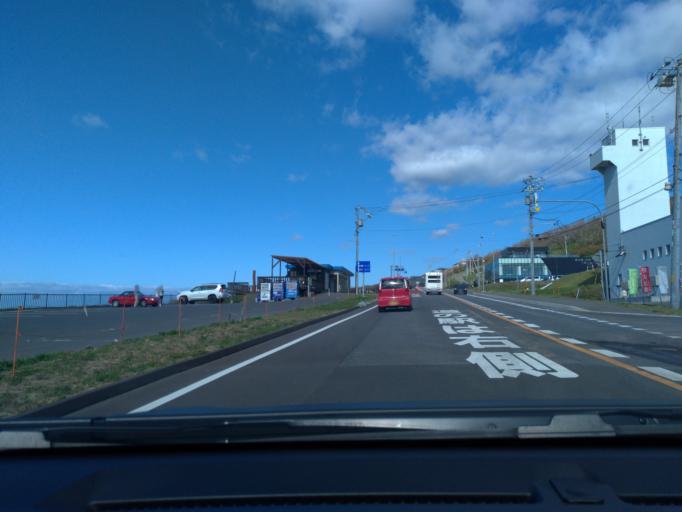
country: JP
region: Hokkaido
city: Ishikari
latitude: 43.4026
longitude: 141.4313
